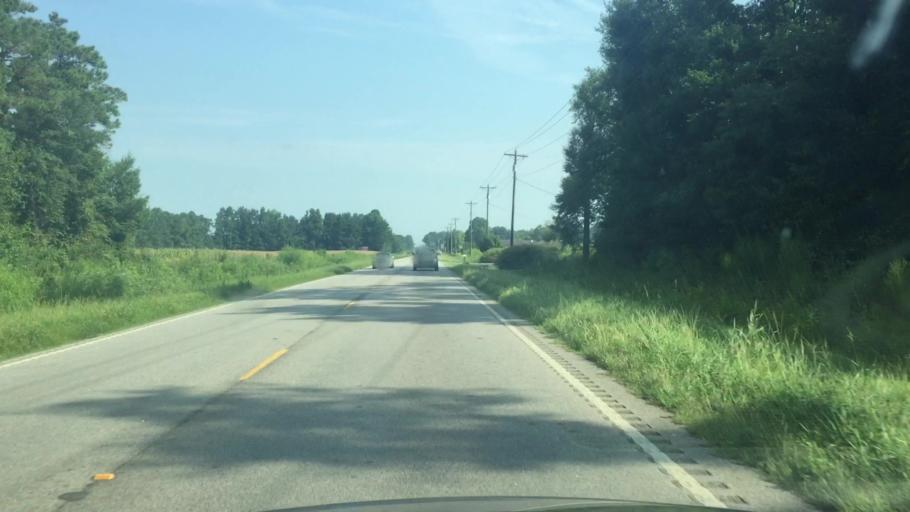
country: US
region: North Carolina
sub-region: Columbus County
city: Tabor City
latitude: 34.1247
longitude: -78.8759
